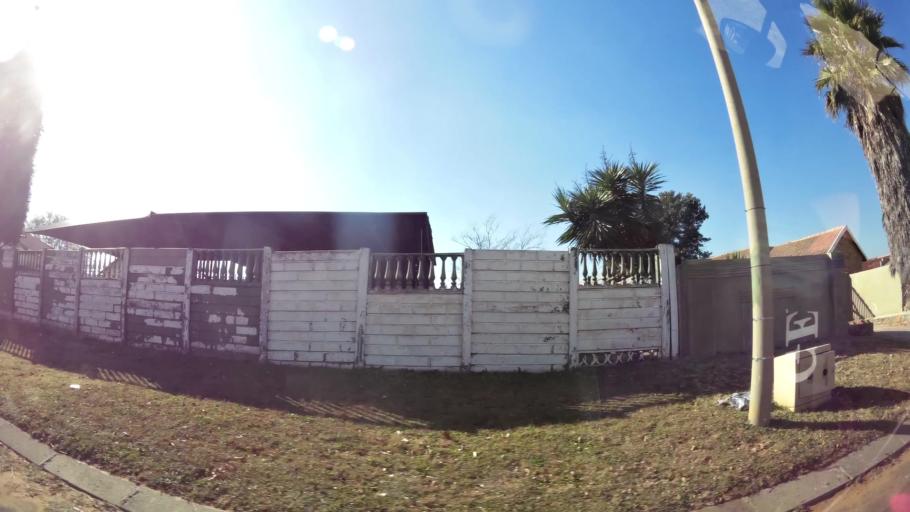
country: ZA
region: Gauteng
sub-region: City of Johannesburg Metropolitan Municipality
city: Roodepoort
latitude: -26.1666
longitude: 27.8270
